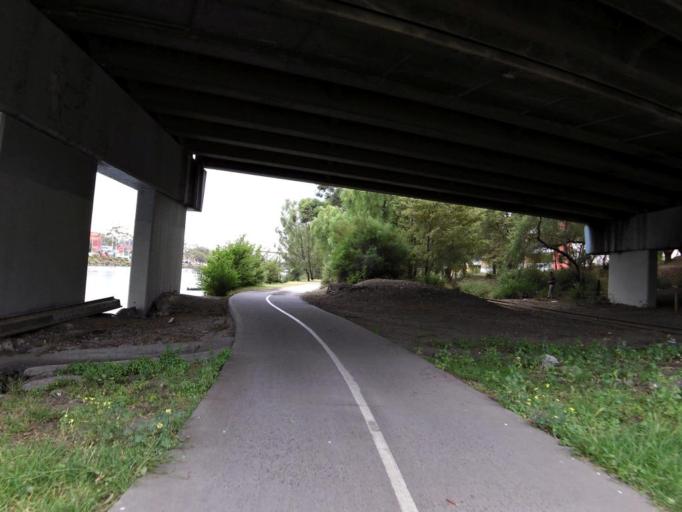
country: AU
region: Victoria
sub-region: Maribyrnong
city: Footscray
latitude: -37.8008
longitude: 144.9098
